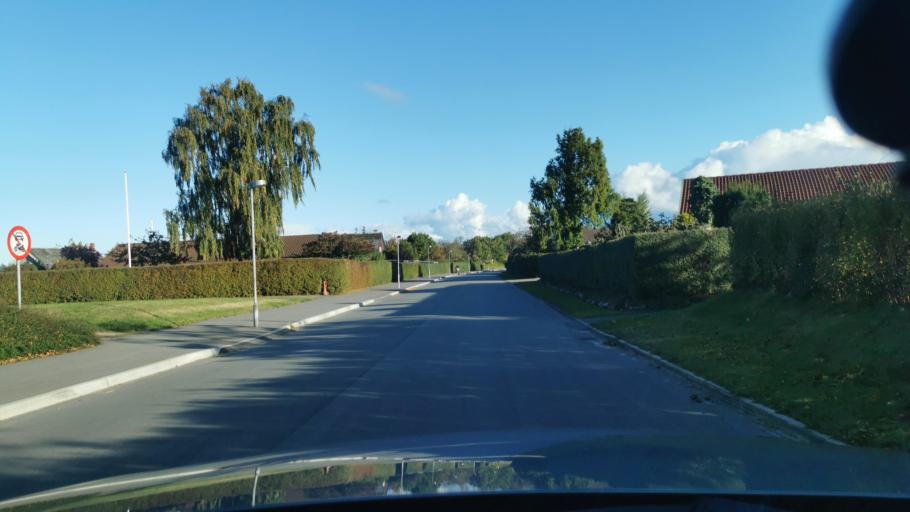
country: DK
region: Zealand
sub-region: Kalundborg Kommune
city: Svebolle
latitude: 55.6498
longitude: 11.2795
